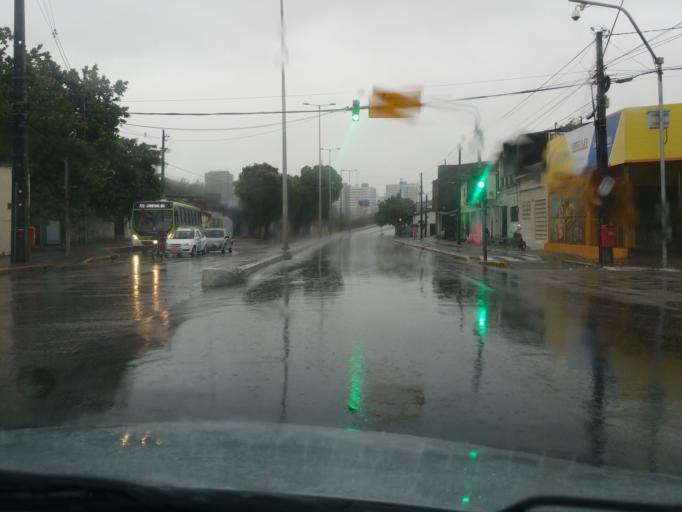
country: BR
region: Pernambuco
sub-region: Recife
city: Recife
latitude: -8.0439
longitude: -34.8823
